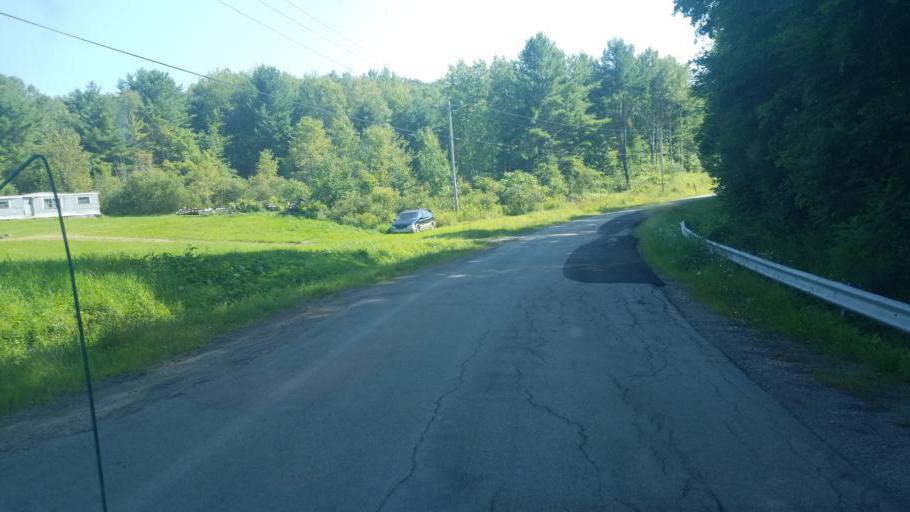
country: US
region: New York
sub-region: Allegany County
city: Bolivar
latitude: 42.0794
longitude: -78.0599
